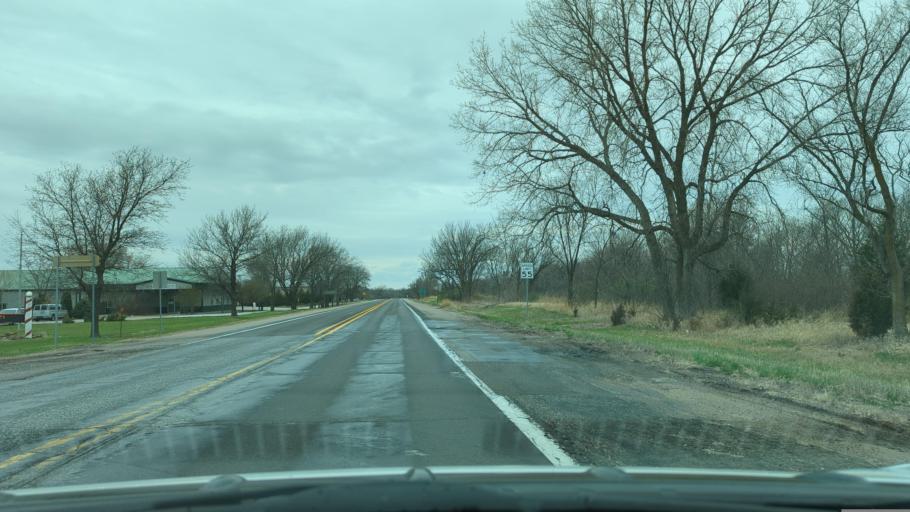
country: US
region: Nebraska
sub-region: Lancaster County
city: Waverly
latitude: 40.9581
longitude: -96.4458
